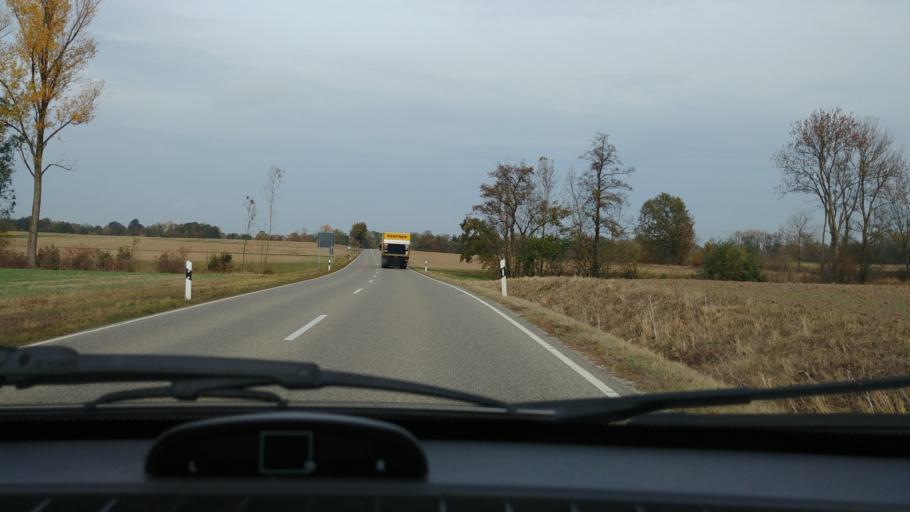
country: DE
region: Baden-Wuerttemberg
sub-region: Regierungsbezirk Stuttgart
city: Stimpfach
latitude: 49.0812
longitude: 10.0697
